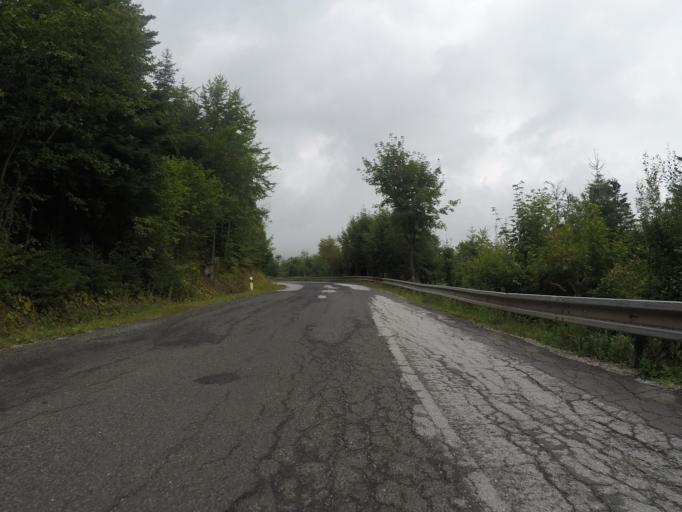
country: SK
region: Kosicky
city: Spisska Nova Ves
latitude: 48.8645
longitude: 20.5281
